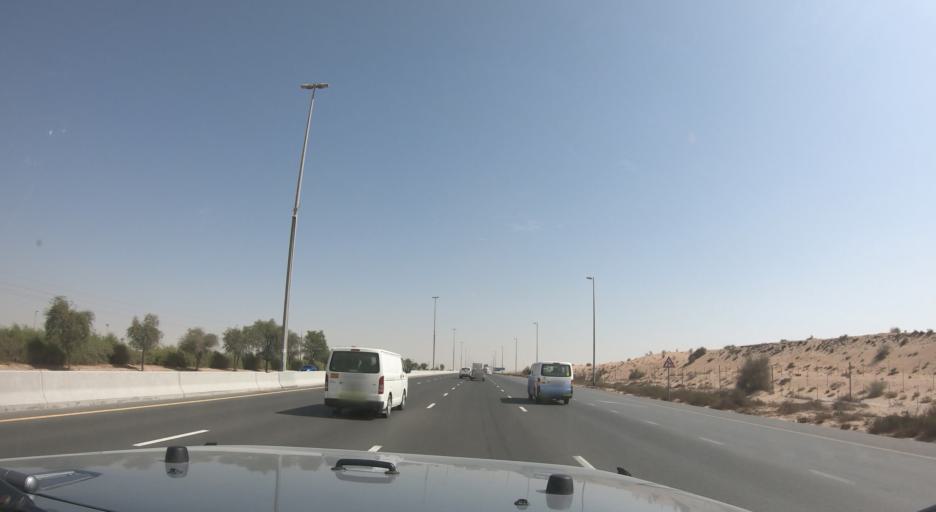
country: AE
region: Ash Shariqah
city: Sharjah
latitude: 25.1648
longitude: 55.4843
